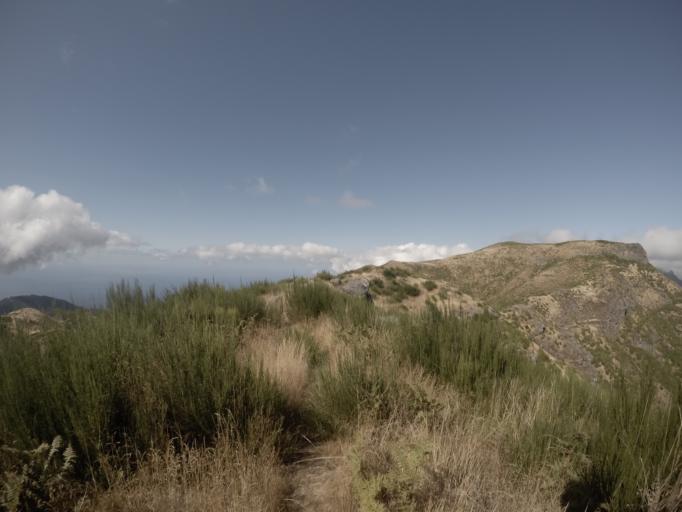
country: PT
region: Madeira
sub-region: Camara de Lobos
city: Curral das Freiras
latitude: 32.7151
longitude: -16.9954
